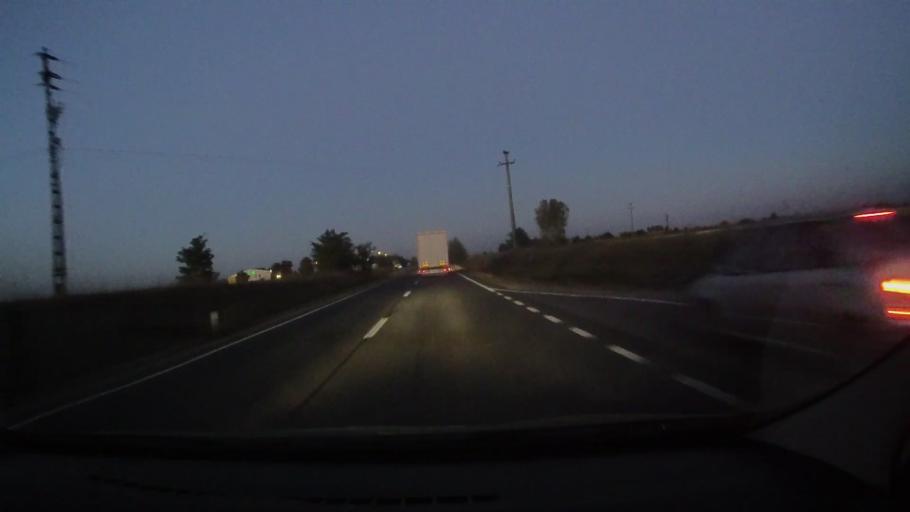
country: RO
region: Bihor
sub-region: Comuna Valea lui Mihai
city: Valea lui Mihai
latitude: 47.5197
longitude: 22.1692
